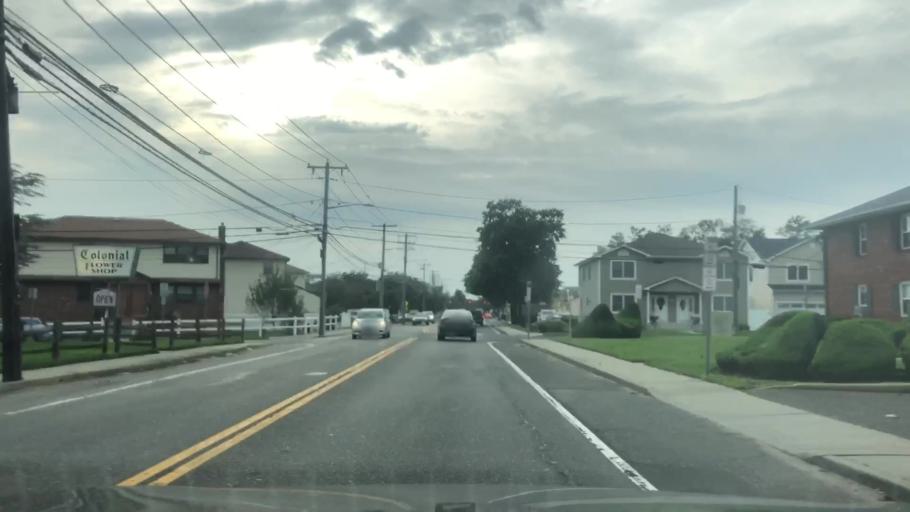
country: US
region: New York
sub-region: Nassau County
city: North Bellmore
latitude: 40.6913
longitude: -73.5391
